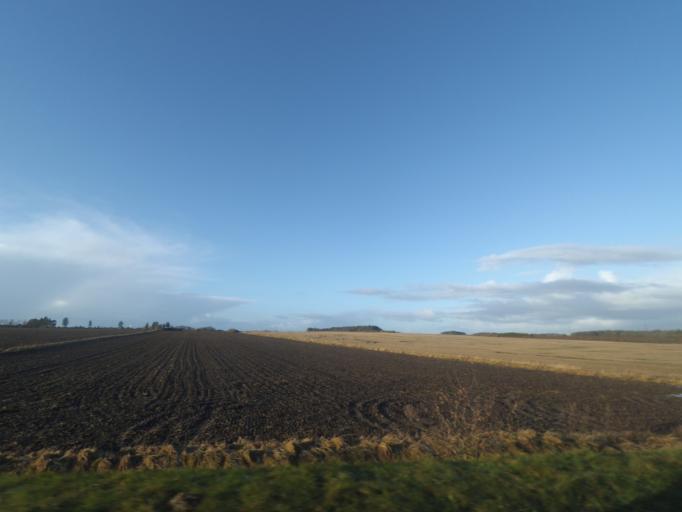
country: DK
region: Central Jutland
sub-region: Ikast-Brande Kommune
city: Ikast
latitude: 56.1107
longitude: 9.1382
